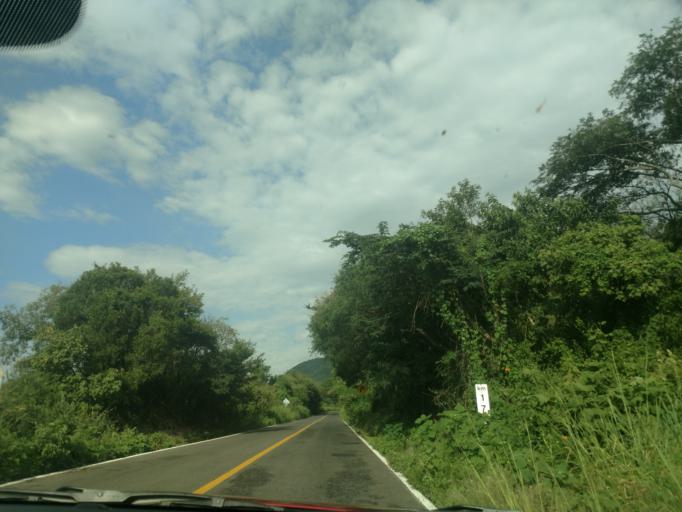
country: MX
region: Jalisco
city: Ameca
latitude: 20.5346
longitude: -104.1868
